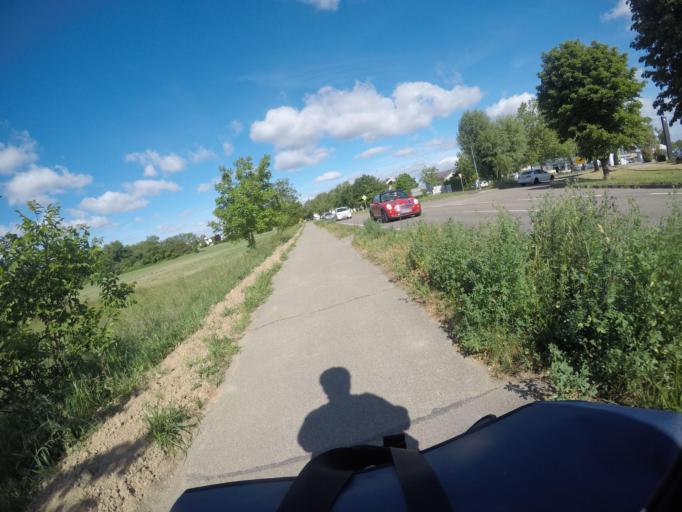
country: DE
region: Baden-Wuerttemberg
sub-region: Karlsruhe Region
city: Durmersheim
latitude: 48.9399
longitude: 8.2627
